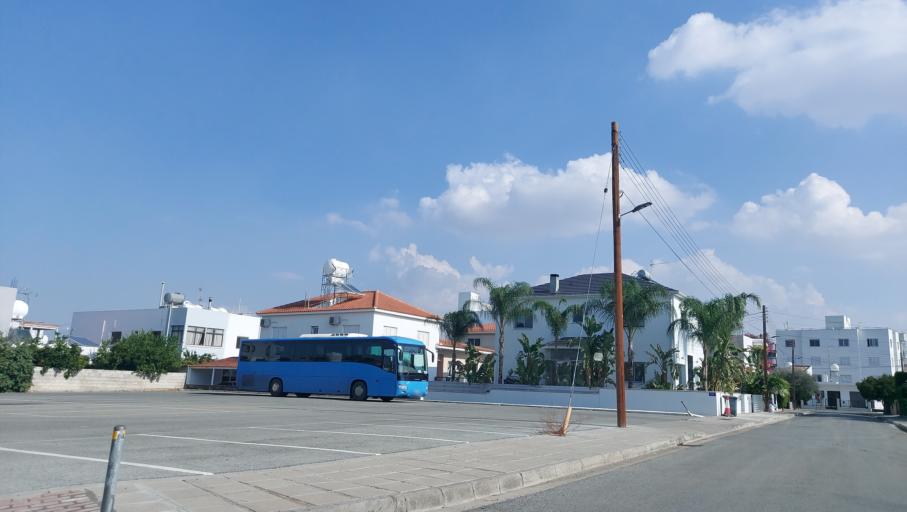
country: CY
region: Lefkosia
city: Kato Deftera
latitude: 35.1061
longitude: 33.3044
